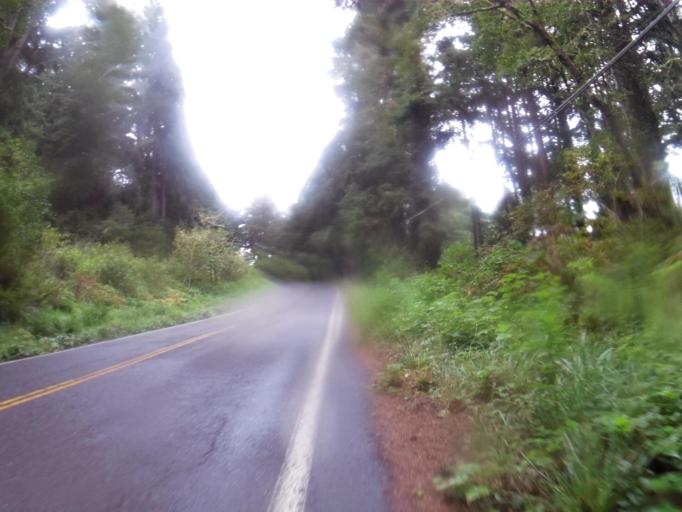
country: US
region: California
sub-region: Humboldt County
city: Westhaven-Moonstone
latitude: 41.1184
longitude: -124.1568
